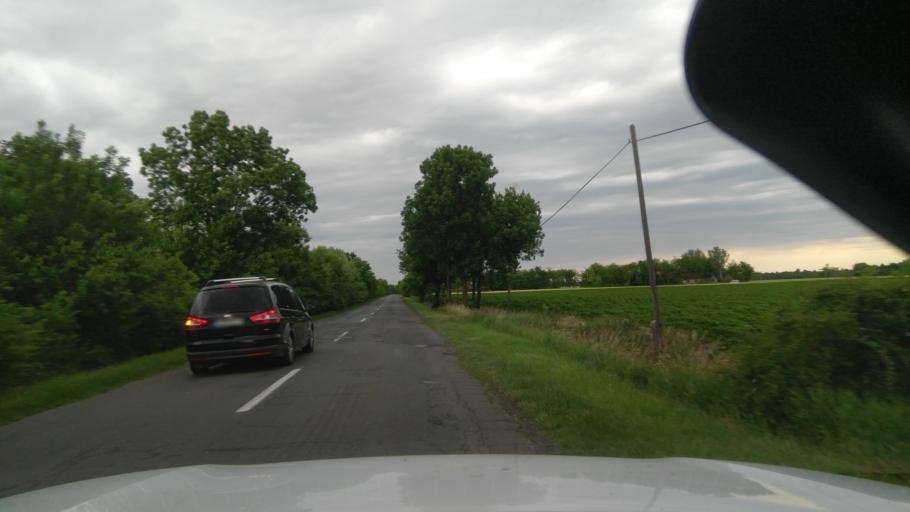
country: HU
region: Bekes
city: Bekescsaba
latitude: 46.6859
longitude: 21.1668
